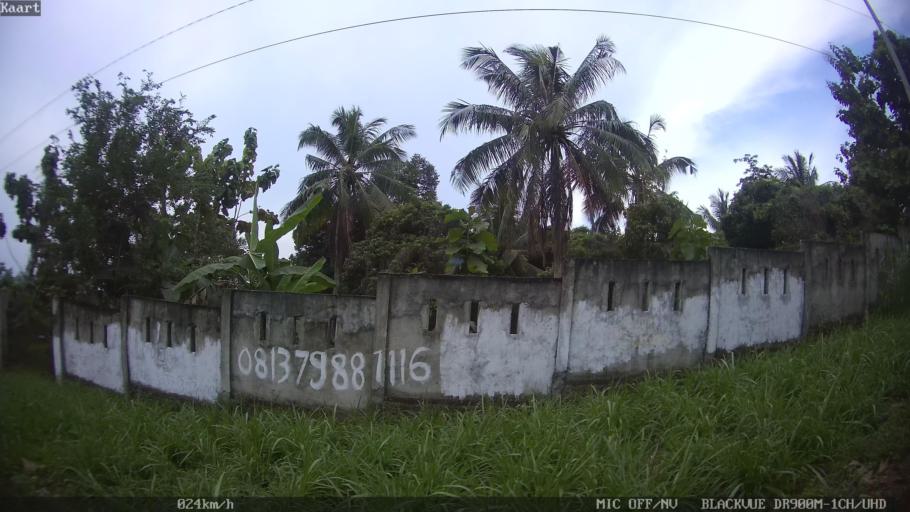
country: ID
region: Lampung
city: Kedaton
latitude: -5.3989
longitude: 105.1926
